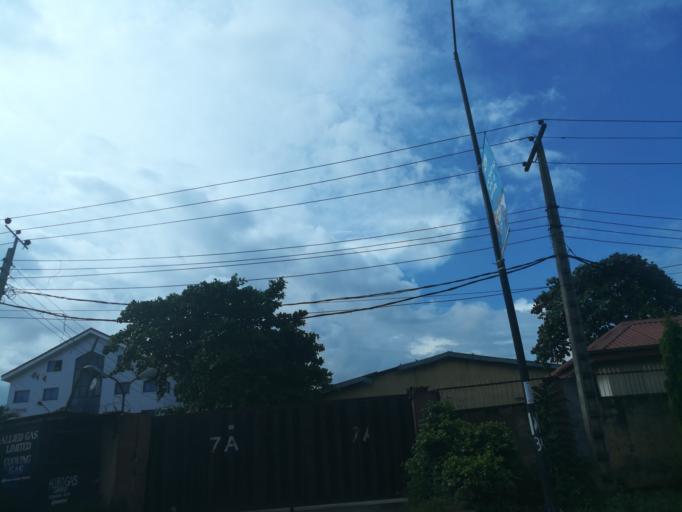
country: NG
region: Lagos
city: Agege
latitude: 6.6254
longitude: 3.3446
